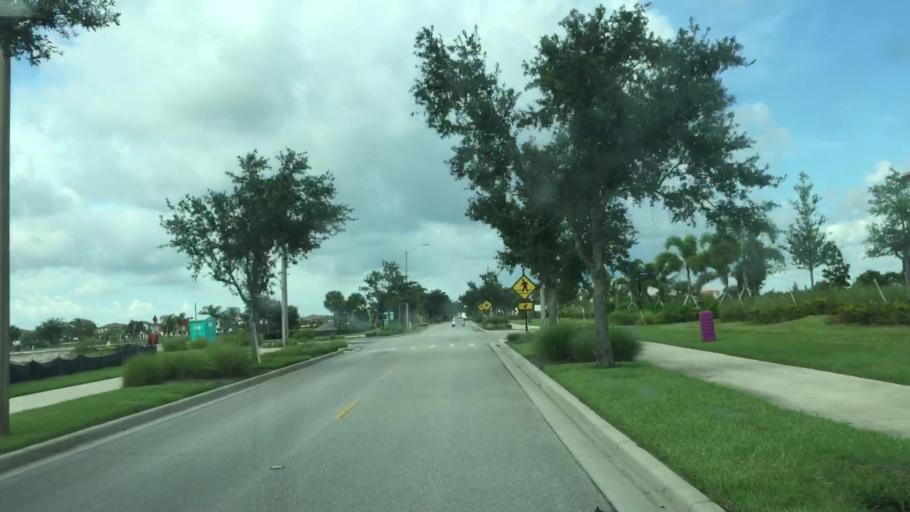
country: US
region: Florida
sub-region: Collier County
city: Immokalee
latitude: 26.3377
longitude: -81.4282
